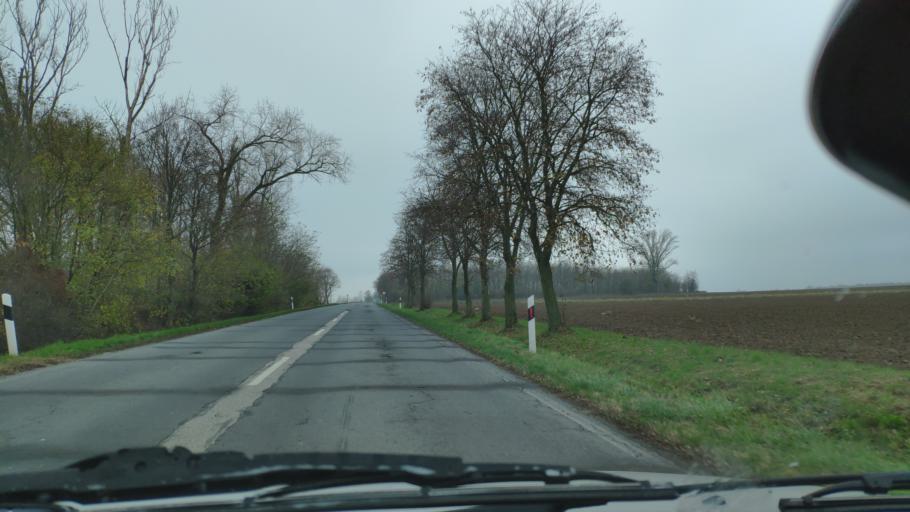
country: HU
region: Zala
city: Zalakomar
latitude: 46.5767
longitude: 17.2633
